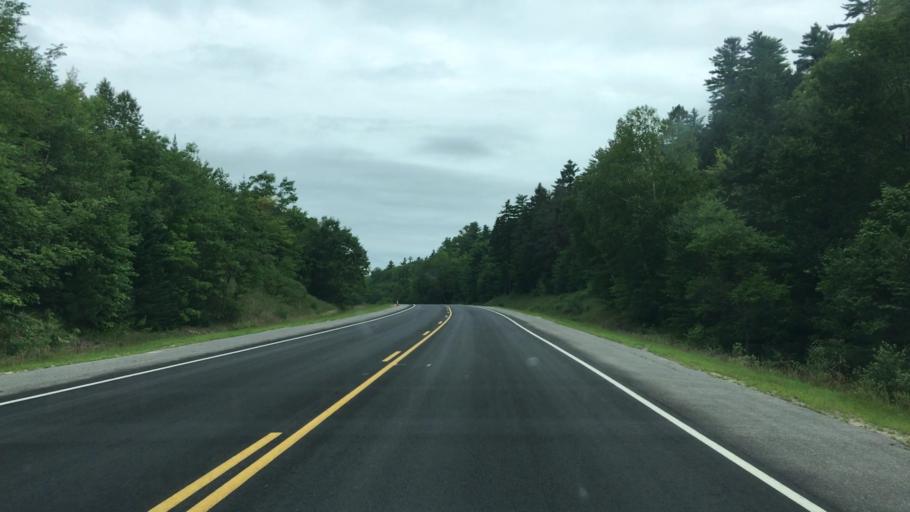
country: US
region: Maine
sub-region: Washington County
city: Cherryfield
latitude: 44.8973
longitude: -67.8557
